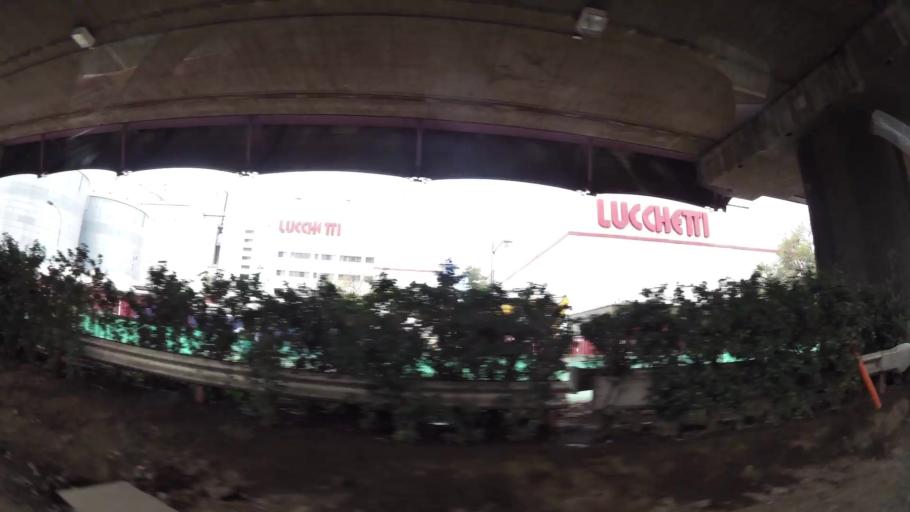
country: CL
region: Santiago Metropolitan
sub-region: Provincia de Santiago
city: Santiago
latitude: -33.4772
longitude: -70.6226
